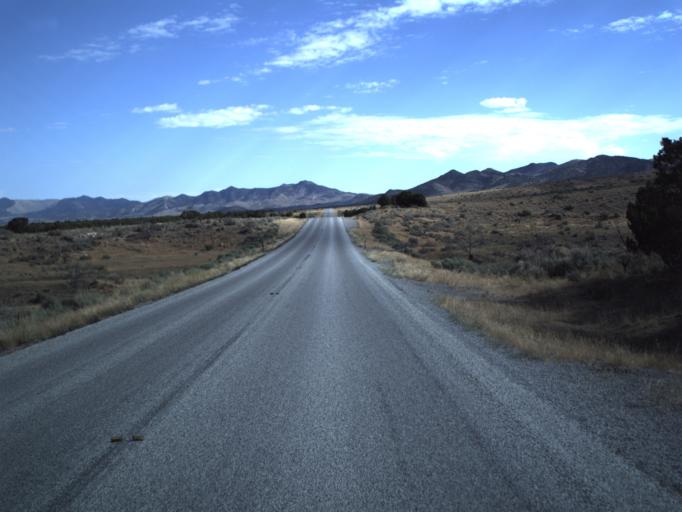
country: US
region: Utah
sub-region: Juab County
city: Mona
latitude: 39.7817
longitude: -112.1519
